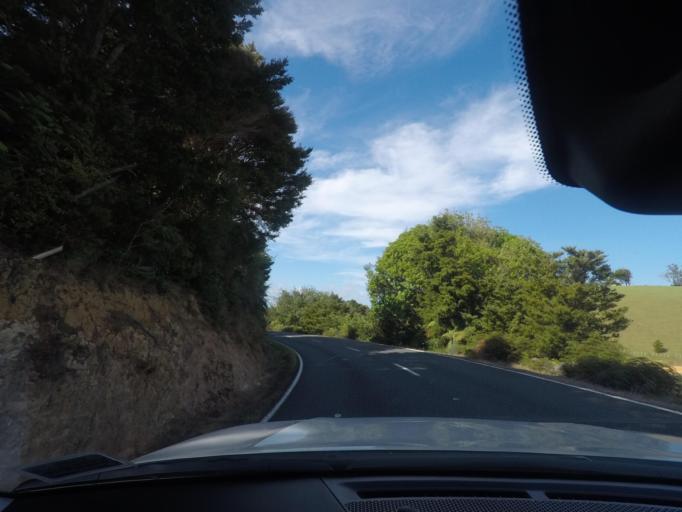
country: NZ
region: Northland
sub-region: Whangarei
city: Ngunguru
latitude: -35.6714
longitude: 174.4700
